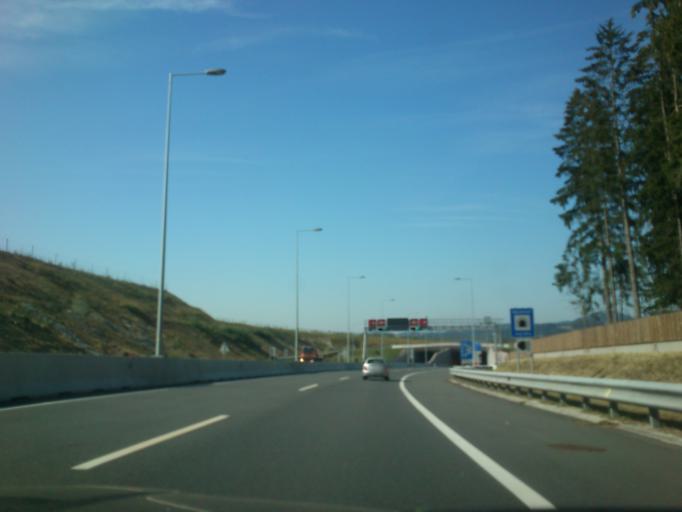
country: AT
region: Upper Austria
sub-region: Politischer Bezirk Freistadt
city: Freistadt
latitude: 48.4930
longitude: 14.5153
